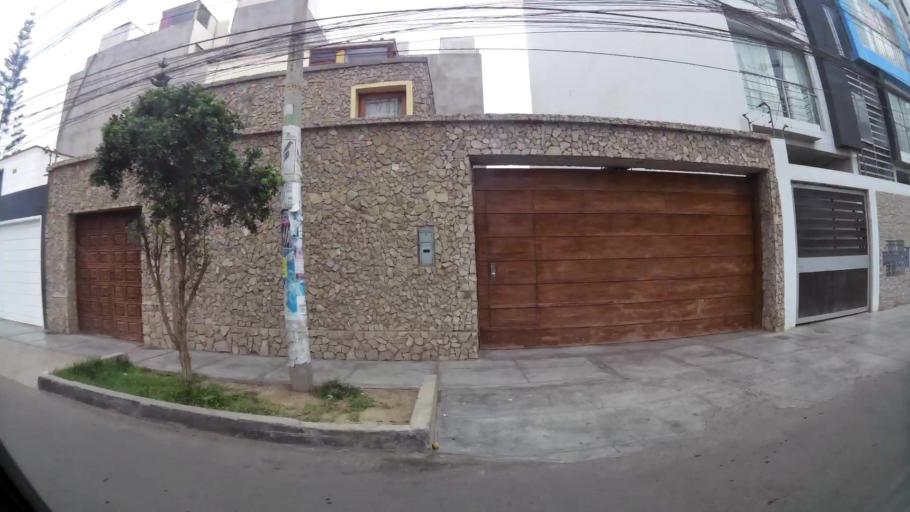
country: PE
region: La Libertad
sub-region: Provincia de Trujillo
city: Buenos Aires
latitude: -8.1333
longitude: -79.0405
